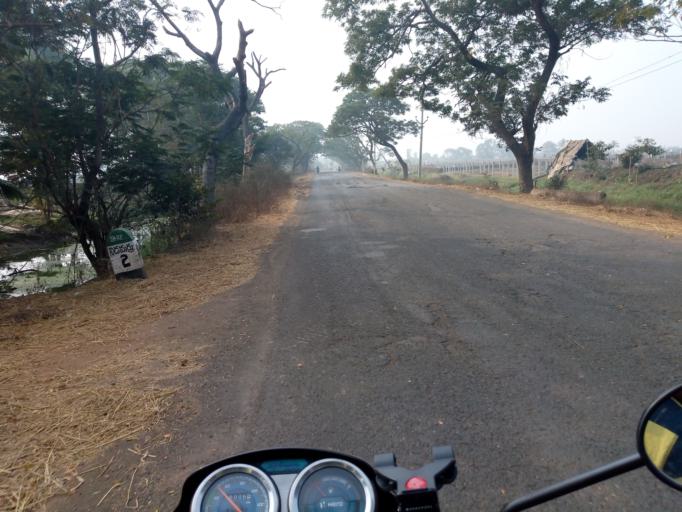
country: IN
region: Andhra Pradesh
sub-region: West Godavari
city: Tadepallegudem
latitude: 16.7490
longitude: 81.4215
